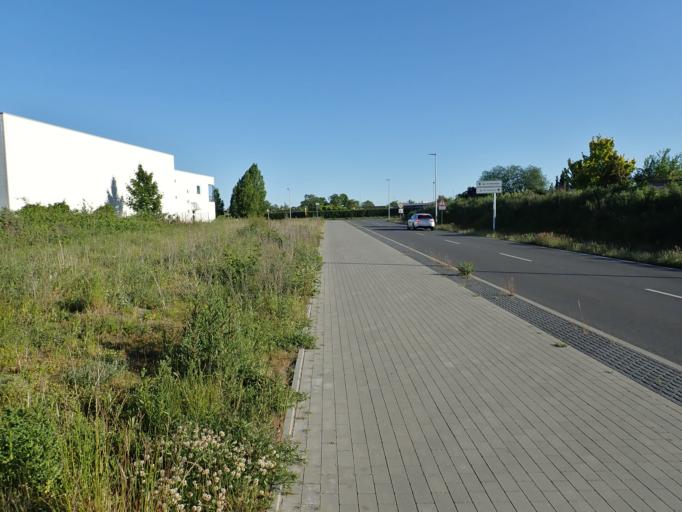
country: DE
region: Mecklenburg-Vorpommern
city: Lambrechtshagen
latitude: 54.1148
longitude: 12.0695
